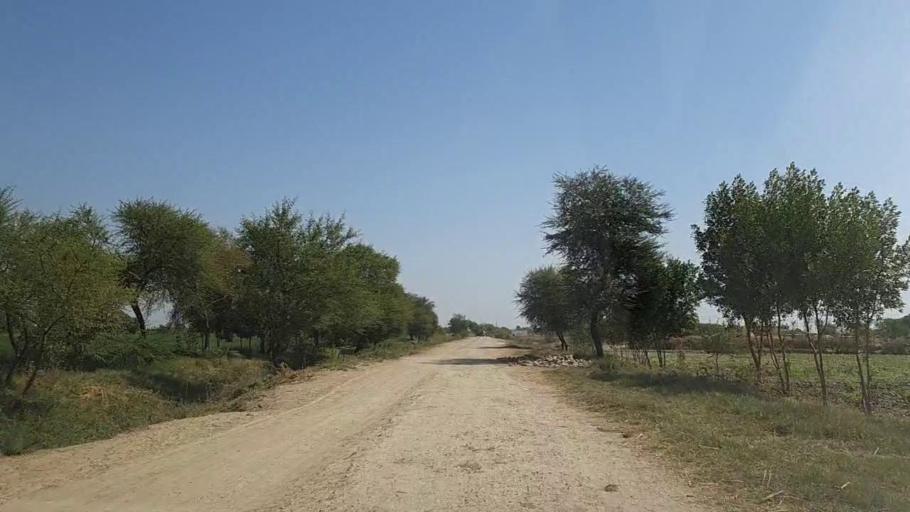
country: PK
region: Sindh
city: Samaro
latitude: 25.2148
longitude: 69.4095
